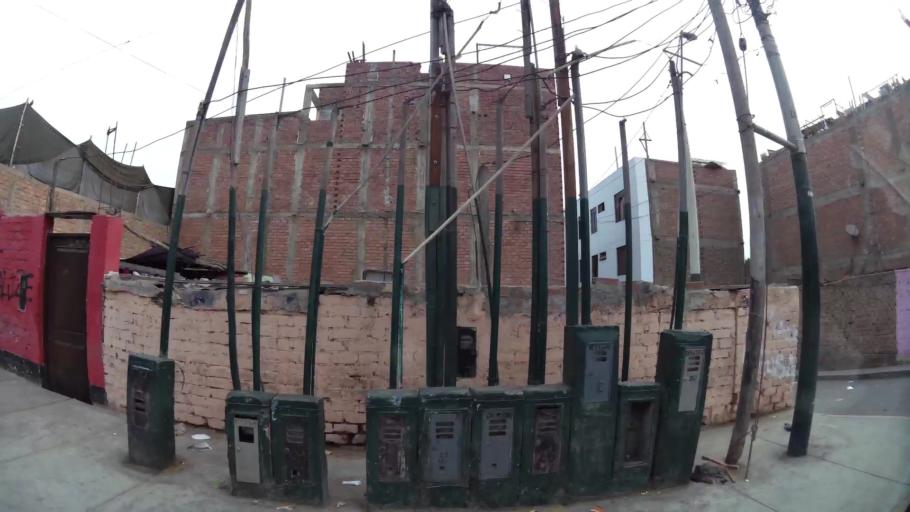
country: PE
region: Lima
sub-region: Lima
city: Surco
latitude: -12.1446
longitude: -77.0121
